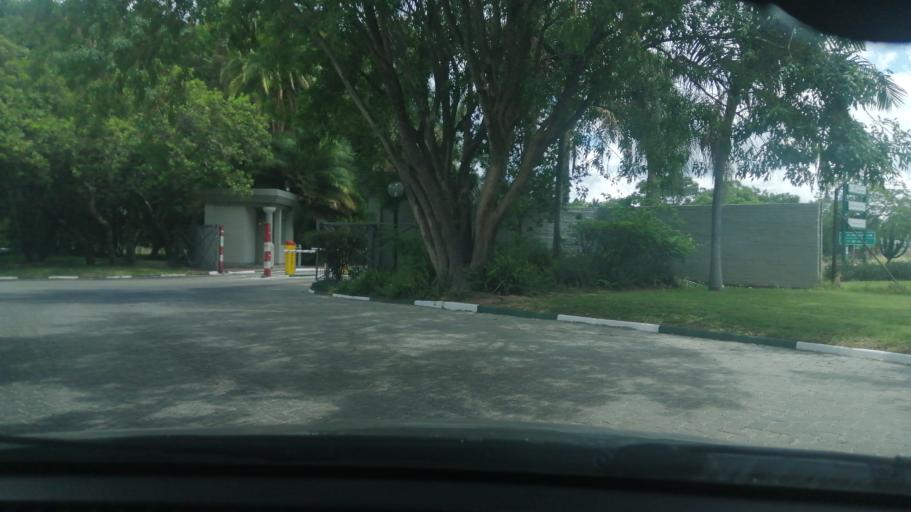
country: ZW
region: Harare
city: Harare
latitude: -17.8326
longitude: 31.1016
